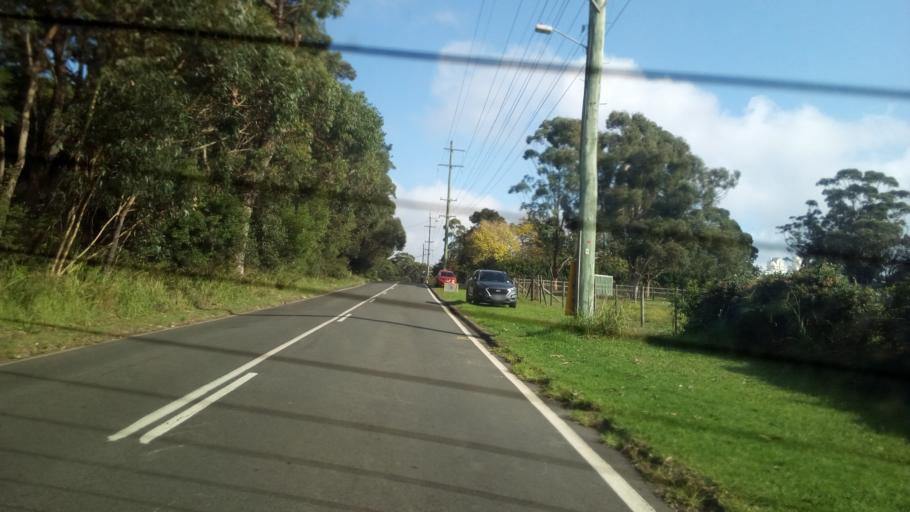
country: AU
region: New South Wales
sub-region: Wollongong
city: Helensburgh
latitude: -34.2095
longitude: 150.9778
